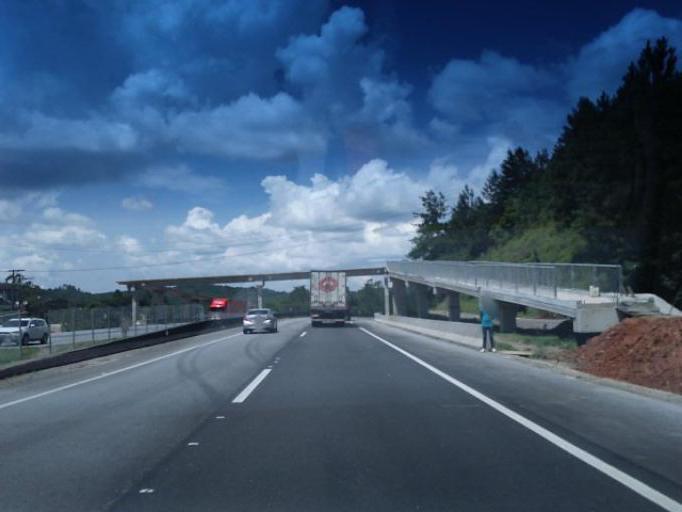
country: BR
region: Sao Paulo
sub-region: Juquitiba
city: Juquitiba
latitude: -23.9372
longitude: -47.0818
